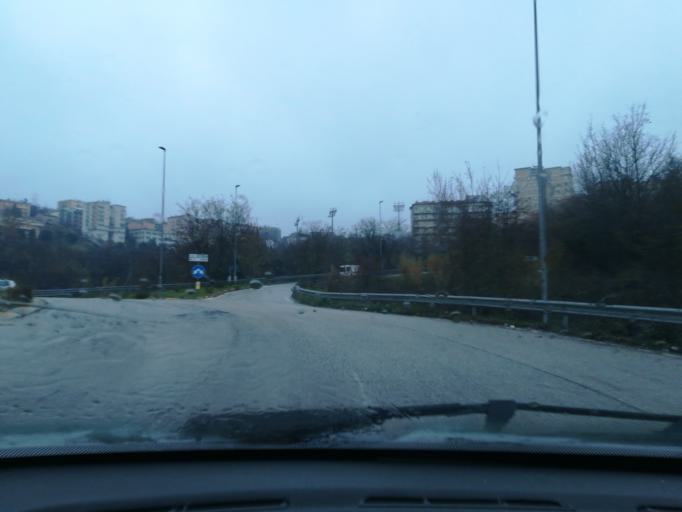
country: IT
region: The Marches
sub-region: Provincia di Macerata
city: Macerata
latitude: 43.2955
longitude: 13.4426
